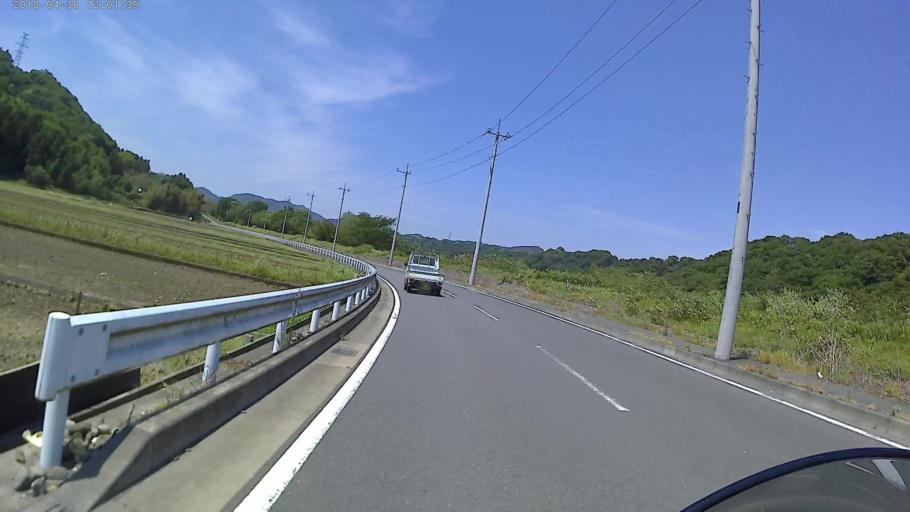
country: JP
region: Kanagawa
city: Zama
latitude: 35.5188
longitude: 139.3244
